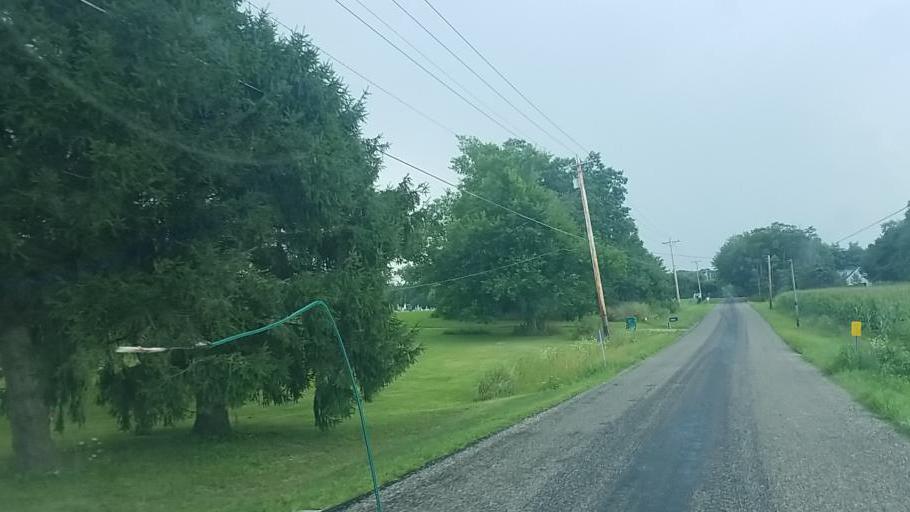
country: US
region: Ohio
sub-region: Medina County
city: Lodi
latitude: 40.9916
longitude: -82.0058
